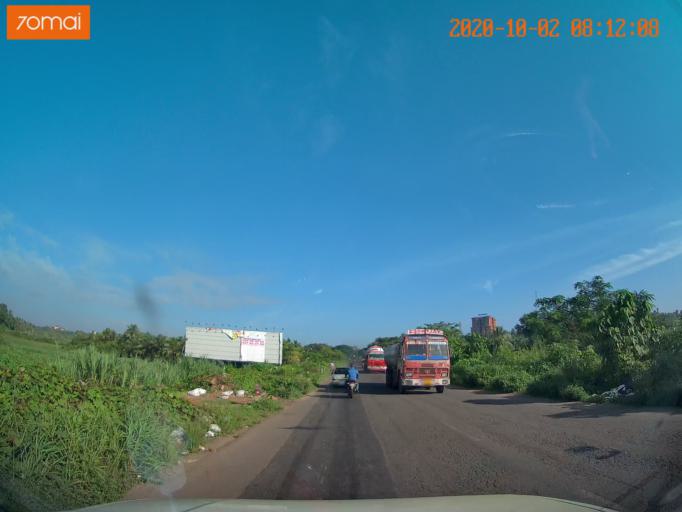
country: IN
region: Kerala
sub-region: Kozhikode
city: Kozhikode
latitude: 11.2790
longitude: 75.8049
